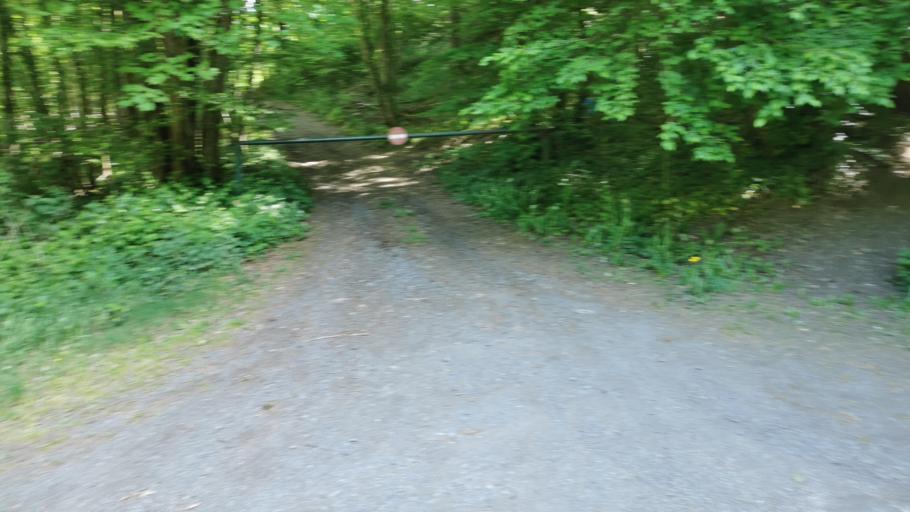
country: FR
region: Nord-Pas-de-Calais
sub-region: Departement du Nord
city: Anor
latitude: 49.9718
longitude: 4.1060
